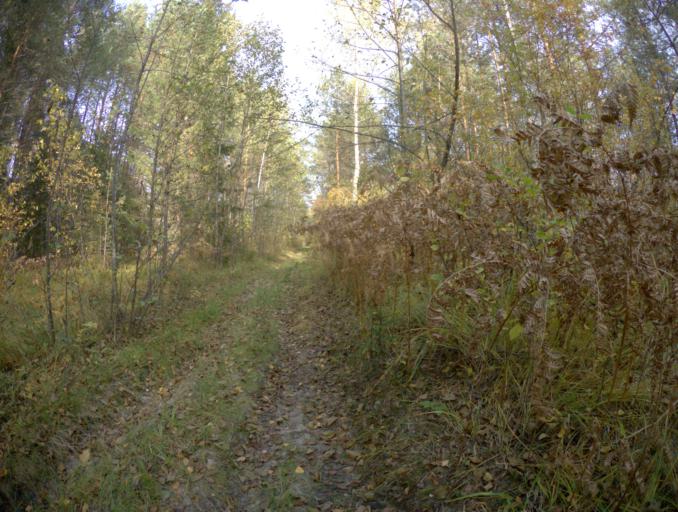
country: RU
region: Vladimir
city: Sobinka
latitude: 55.9351
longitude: 40.0420
